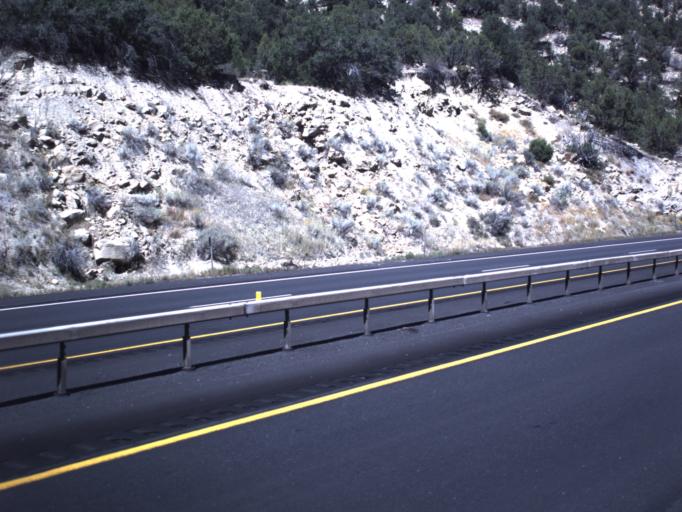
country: US
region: Utah
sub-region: Sevier County
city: Salina
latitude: 38.9020
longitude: -111.6434
